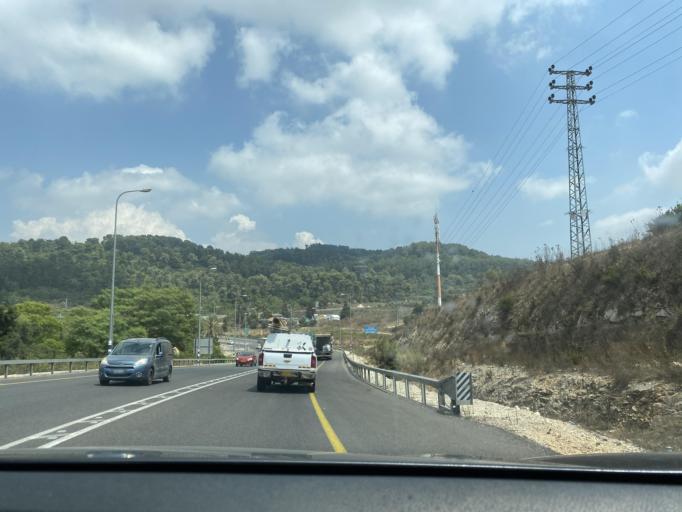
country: IL
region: Northern District
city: Kefar Weradim
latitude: 33.0036
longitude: 35.2920
